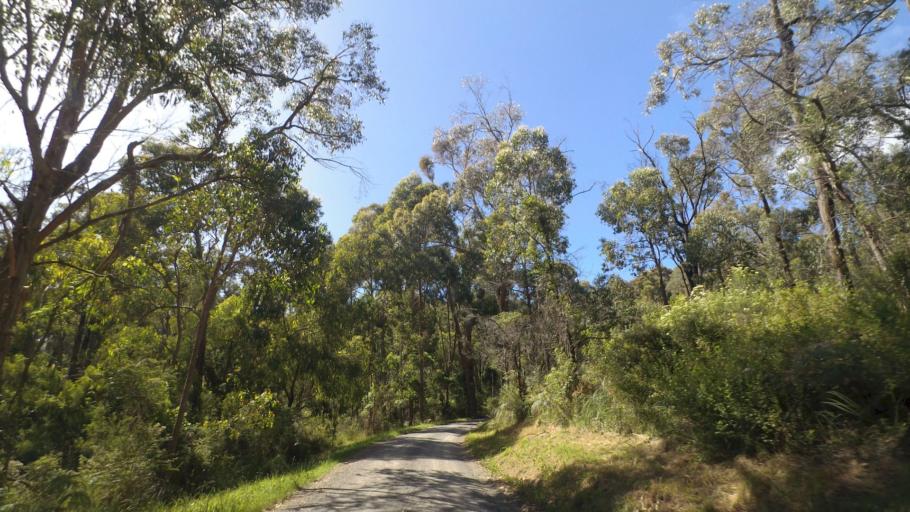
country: AU
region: Victoria
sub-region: Yarra Ranges
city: Kalorama
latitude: -37.8076
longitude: 145.3685
